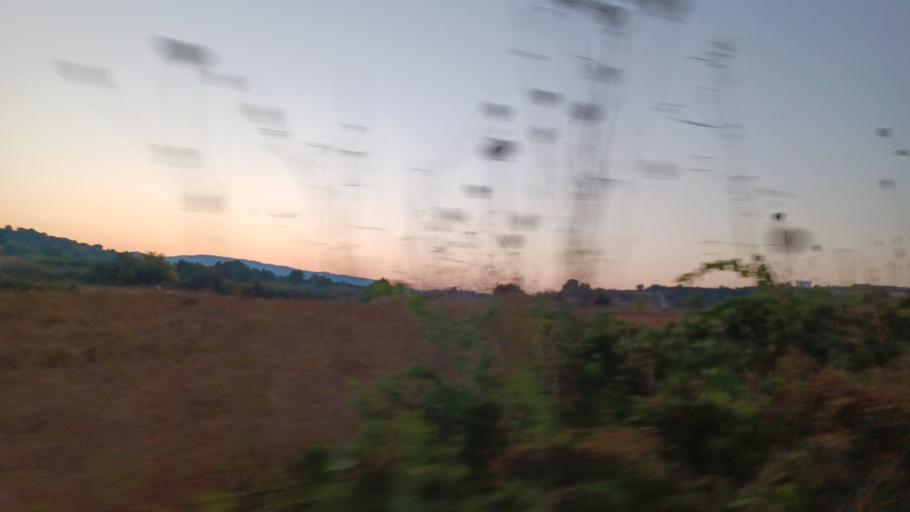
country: CY
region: Pafos
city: Mesogi
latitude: 34.8711
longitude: 32.4969
